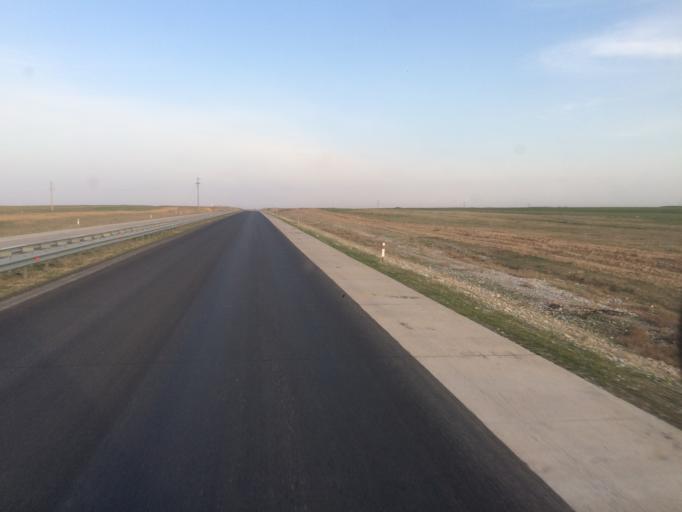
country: KZ
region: Ongtustik Qazaqstan
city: Temirlanovka
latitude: 42.5189
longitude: 69.4129
